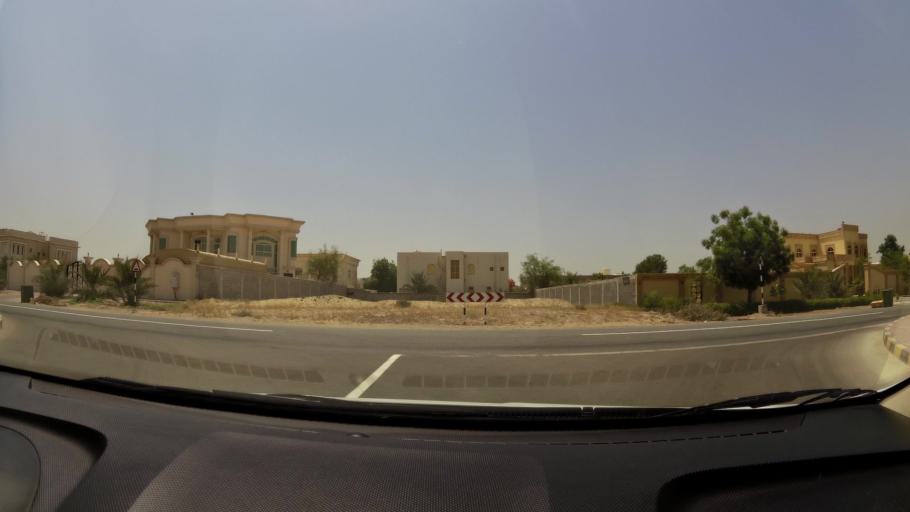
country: AE
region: Ajman
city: Ajman
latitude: 25.4284
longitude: 55.5133
